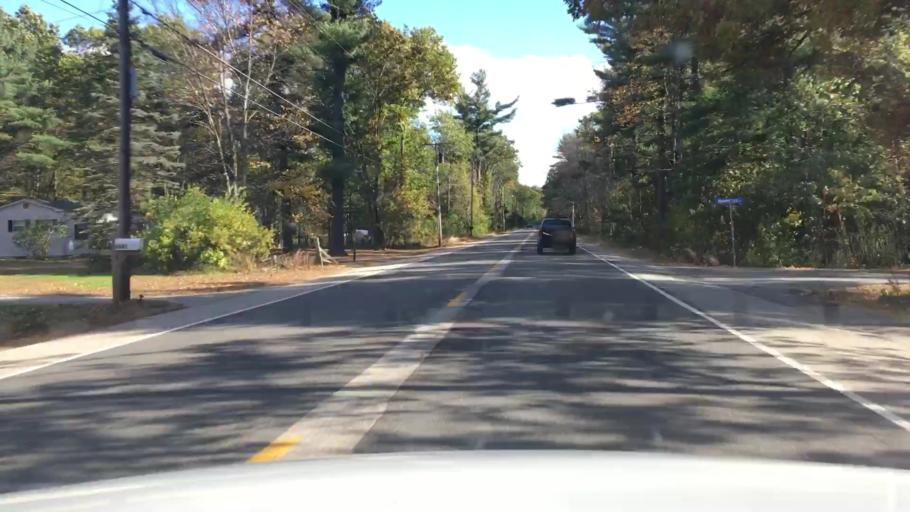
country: US
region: Maine
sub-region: York County
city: South Sanford
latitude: 43.3765
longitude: -70.6800
